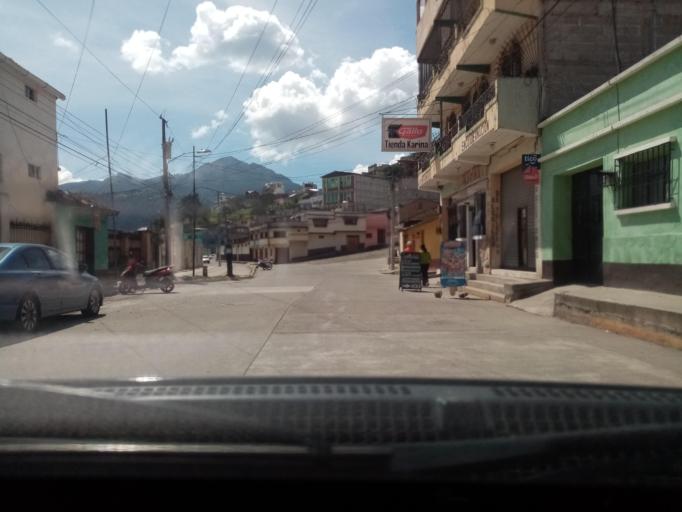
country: GT
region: Quetzaltenango
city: Quetzaltenango
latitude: 14.8415
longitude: -91.5123
